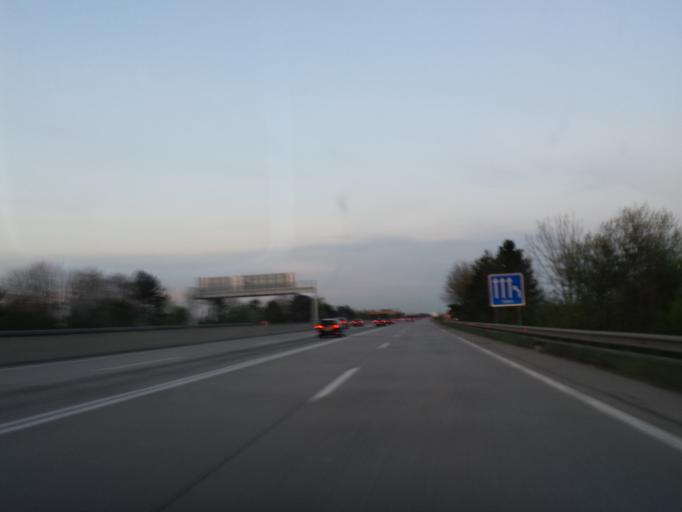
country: AT
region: Lower Austria
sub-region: Politischer Bezirk Neunkirchen
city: Breitenau
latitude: 47.7228
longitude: 16.1419
